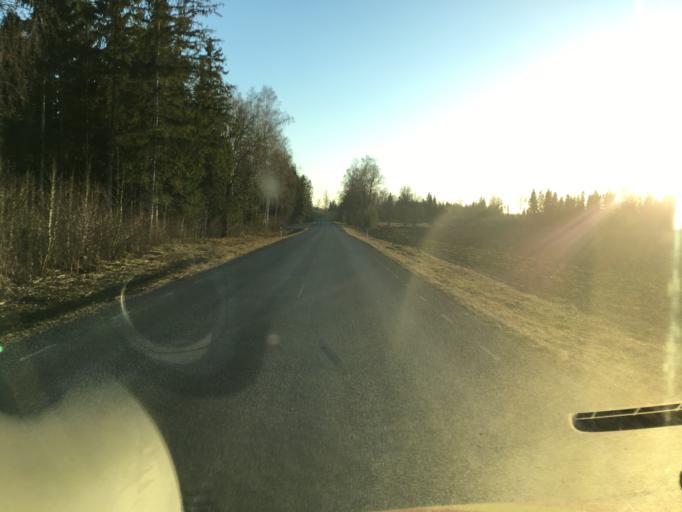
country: EE
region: Raplamaa
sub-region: Kehtna vald
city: Kehtna
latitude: 58.9982
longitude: 24.8672
